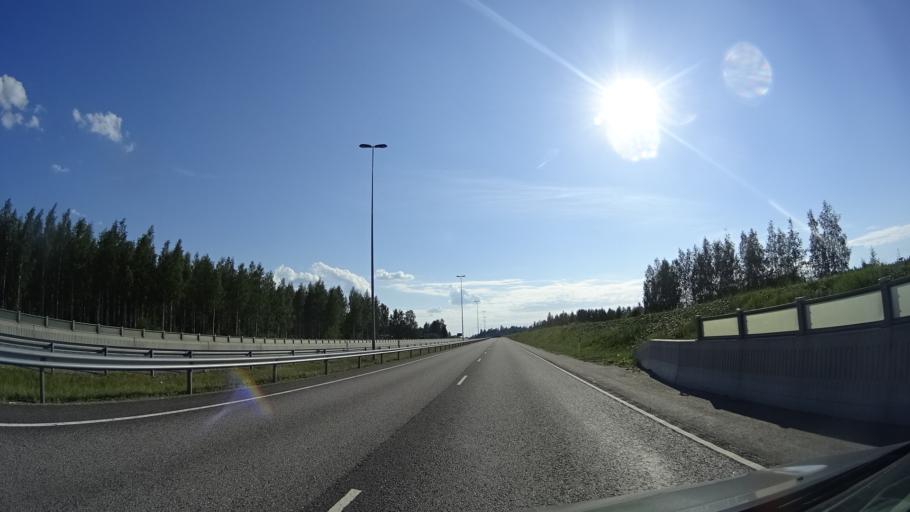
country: FI
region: South Karelia
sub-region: Imatra
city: Imatra
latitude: 61.1786
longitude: 28.7175
